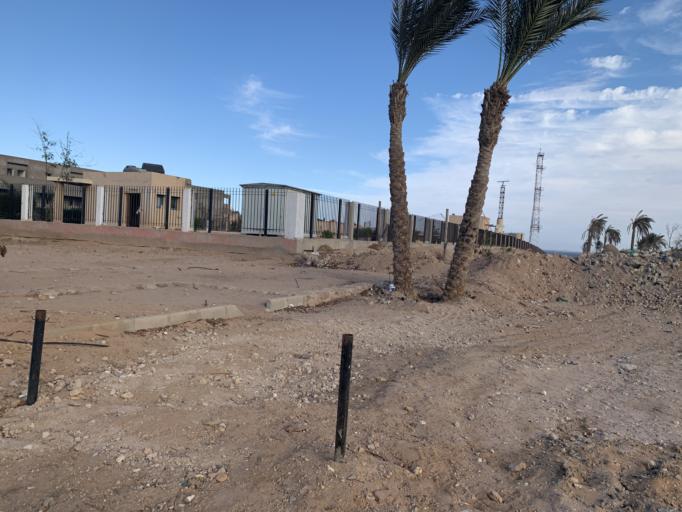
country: EG
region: South Sinai
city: Sharm el-Sheikh
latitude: 28.0176
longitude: 34.4346
